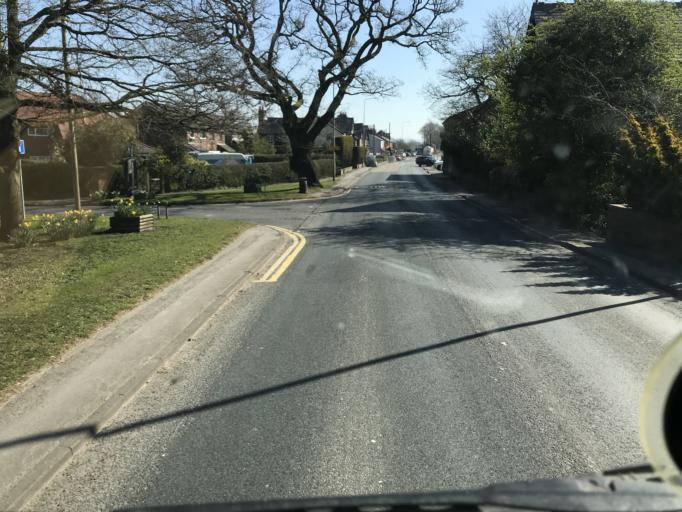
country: GB
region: England
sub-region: Cheshire East
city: Mobberley
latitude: 53.2715
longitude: -2.2852
